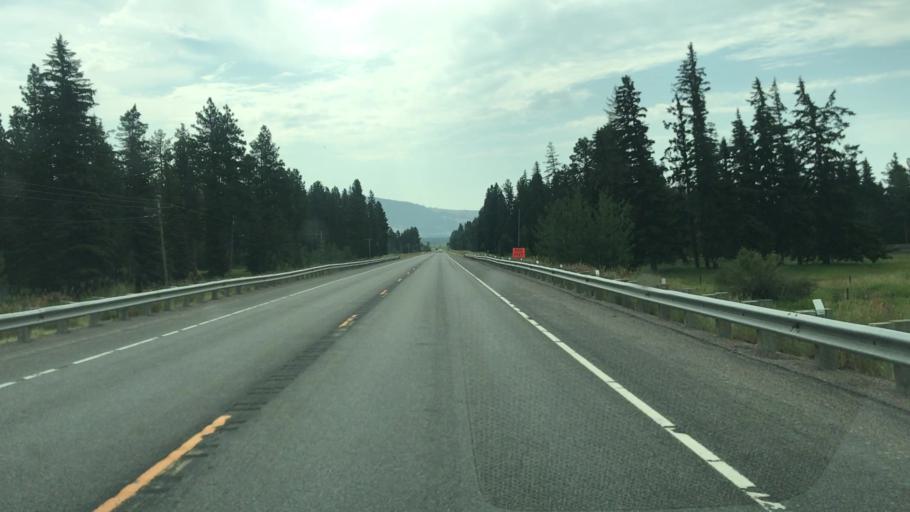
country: US
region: Montana
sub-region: Lewis and Clark County
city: Lincoln
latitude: 47.0052
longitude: -113.0462
